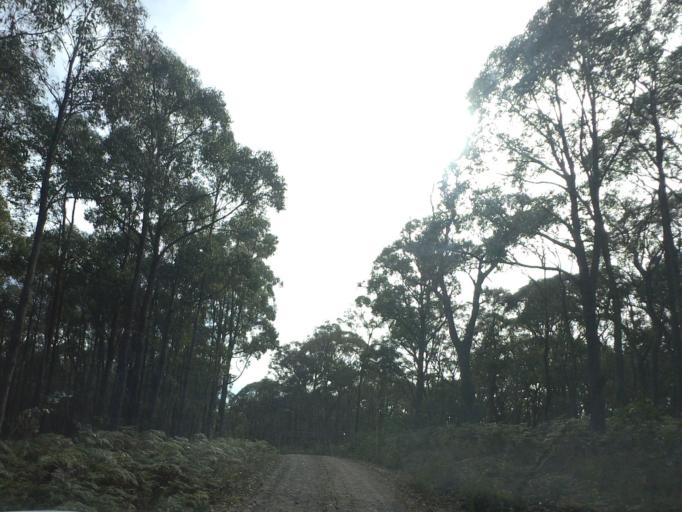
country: AU
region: Victoria
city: Brown Hill
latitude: -37.4914
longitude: 144.1944
